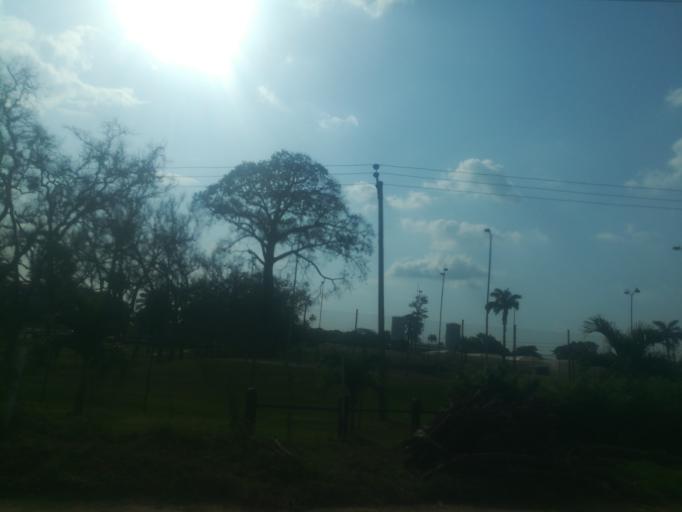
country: NG
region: Oyo
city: Moniya
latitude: 7.5006
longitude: 3.9132
